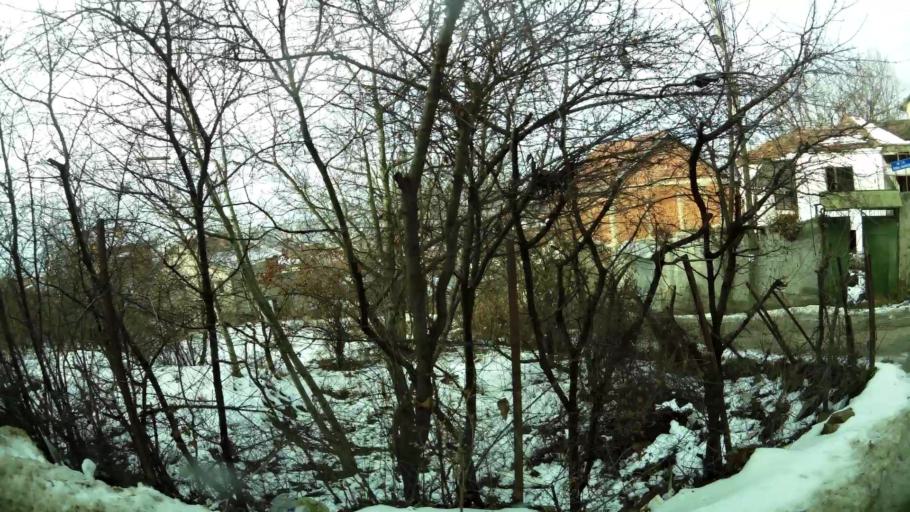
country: XK
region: Pristina
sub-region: Komuna e Prishtines
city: Pristina
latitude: 42.6720
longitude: 21.1753
